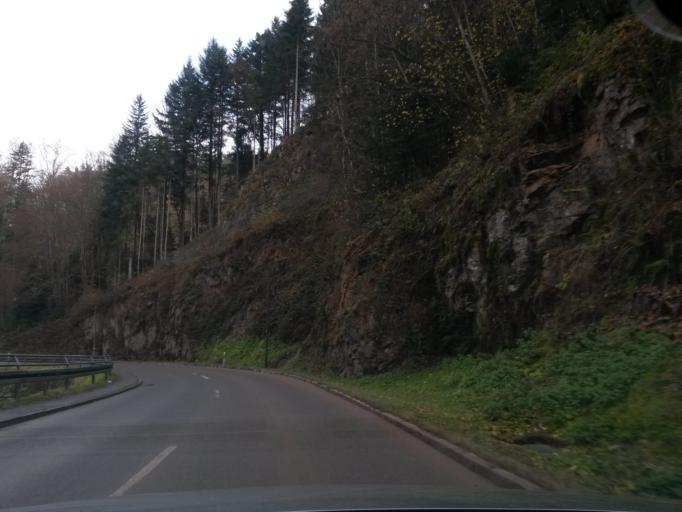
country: DE
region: Baden-Wuerttemberg
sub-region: Freiburg Region
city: Schramberg
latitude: 48.2093
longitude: 8.3799
